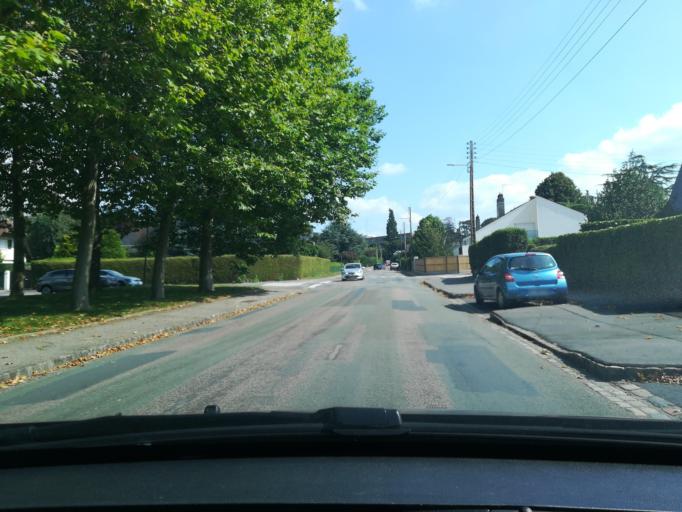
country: FR
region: Haute-Normandie
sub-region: Departement de la Seine-Maritime
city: Bois-Guillaume
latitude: 49.4668
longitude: 1.1114
